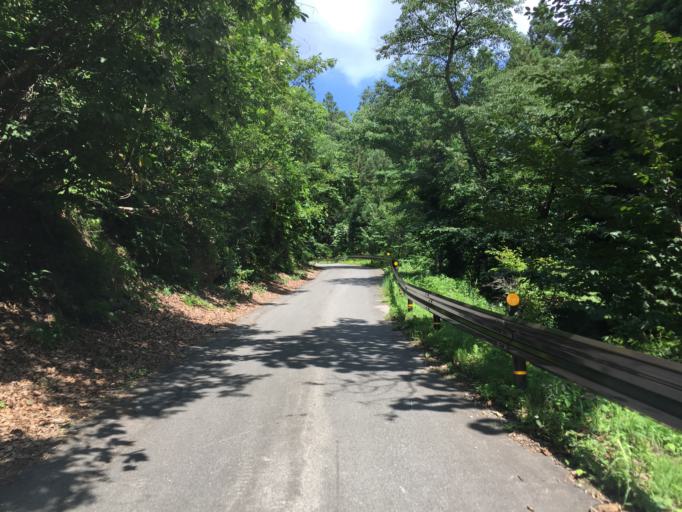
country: JP
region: Fukushima
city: Yanagawamachi-saiwaicho
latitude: 37.7767
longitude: 140.6660
